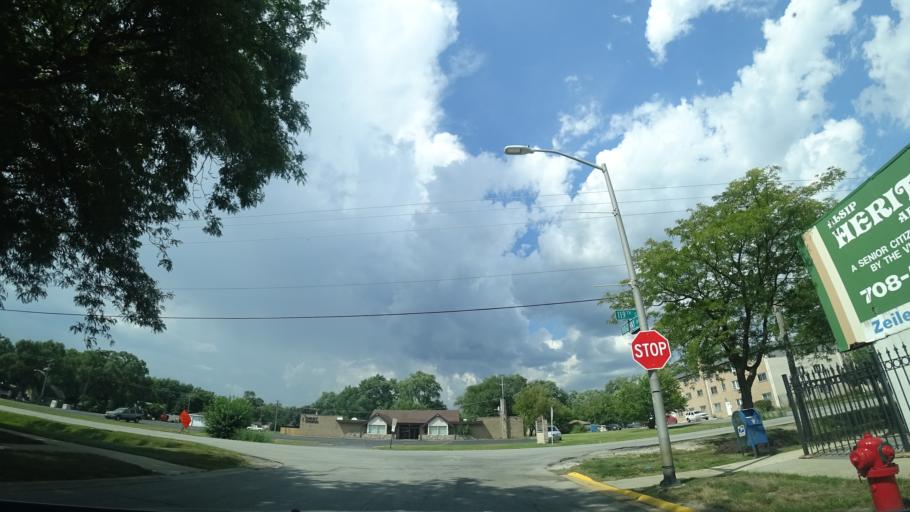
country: US
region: Illinois
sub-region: Cook County
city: Merrionette Park
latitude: 41.6766
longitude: -87.7136
